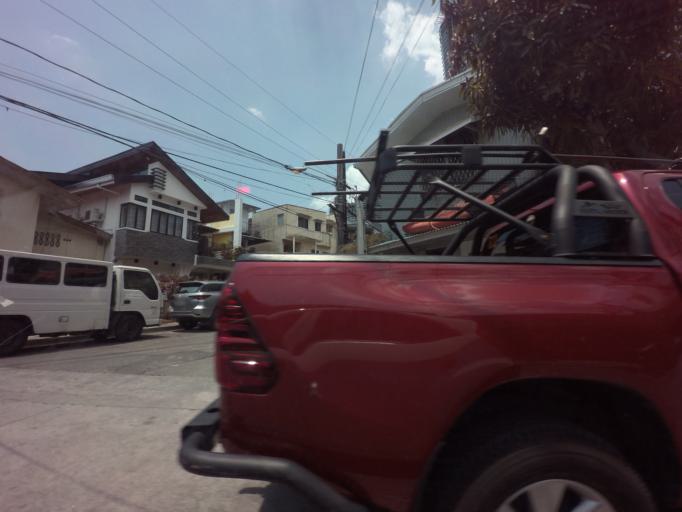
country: PH
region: Metro Manila
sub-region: Mandaluyong
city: Mandaluyong City
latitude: 14.5661
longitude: 121.0406
